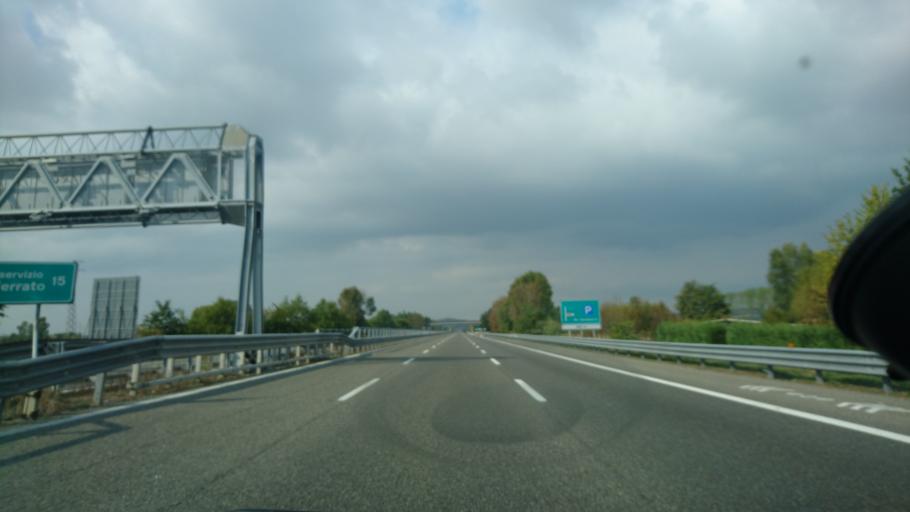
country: IT
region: Piedmont
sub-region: Provincia di Alessandria
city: Castelletto Monferrato
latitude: 44.9462
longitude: 8.5658
